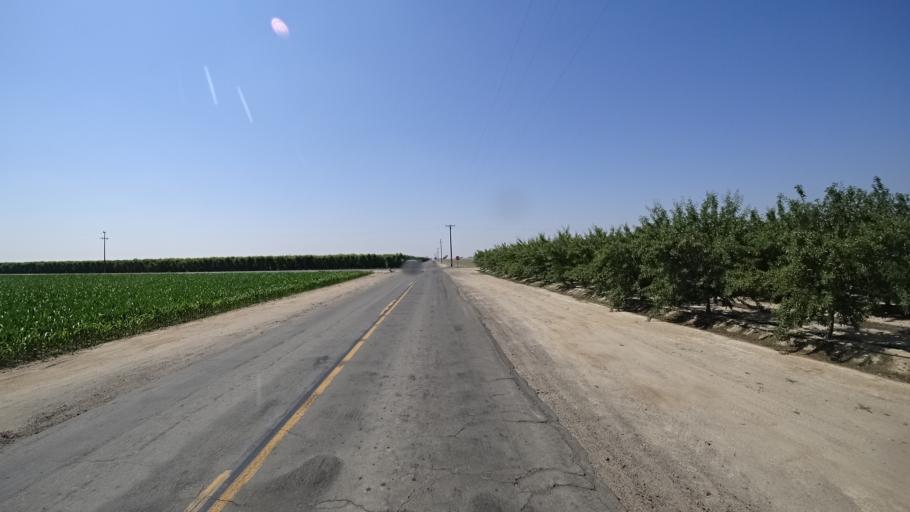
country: US
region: California
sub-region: Fresno County
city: Kingsburg
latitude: 36.4314
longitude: -119.5286
